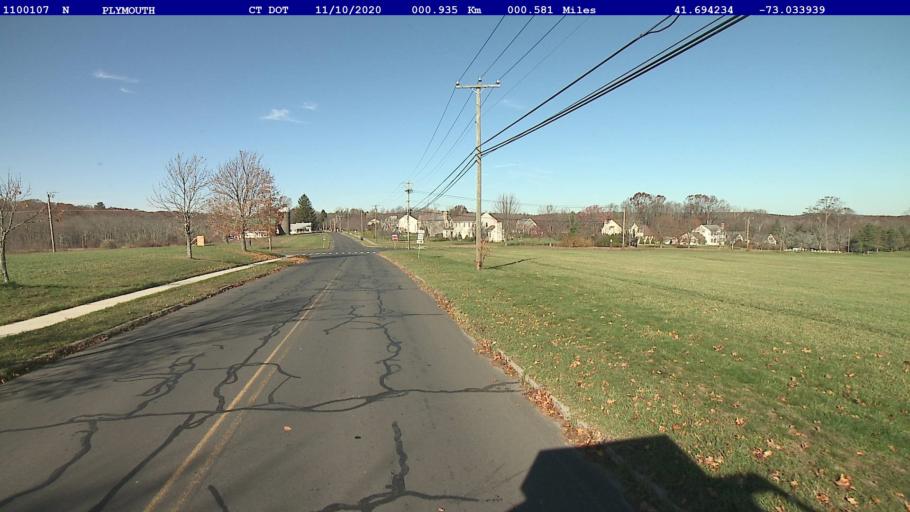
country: US
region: Connecticut
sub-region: Litchfield County
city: Terryville
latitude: 41.6943
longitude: -73.0339
